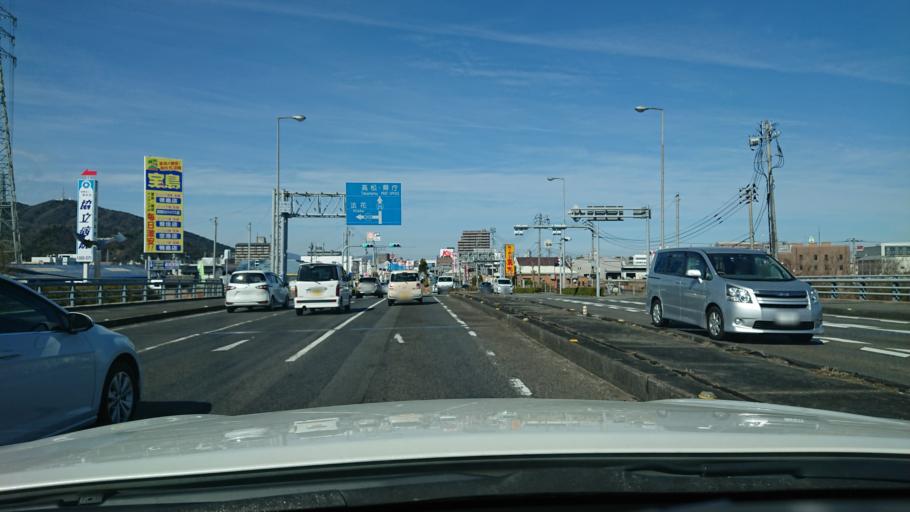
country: JP
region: Tokushima
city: Tokushima-shi
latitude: 34.0447
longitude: 134.5520
